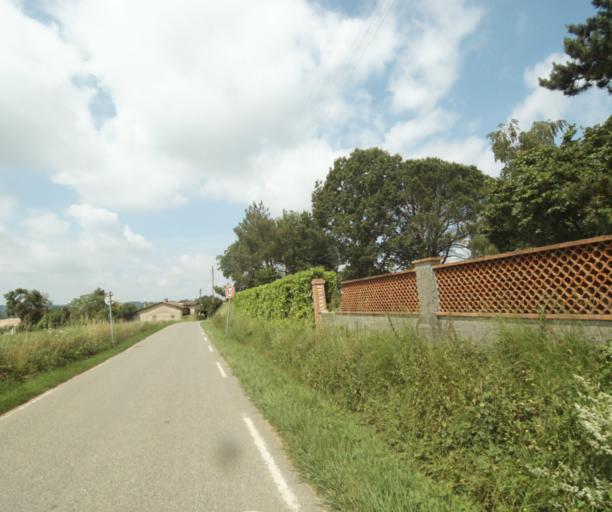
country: FR
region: Midi-Pyrenees
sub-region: Departement du Tarn-et-Garonne
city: Albias
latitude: 44.0695
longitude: 1.4139
